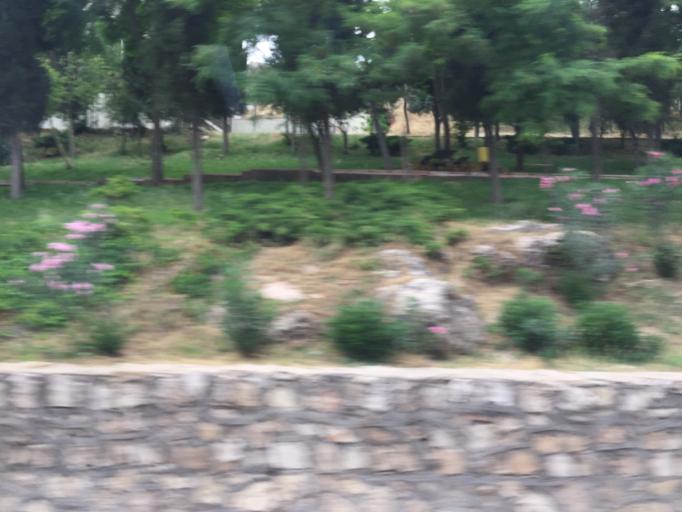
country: TR
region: Gaziantep
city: Gaziantep
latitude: 37.0536
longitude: 37.4192
